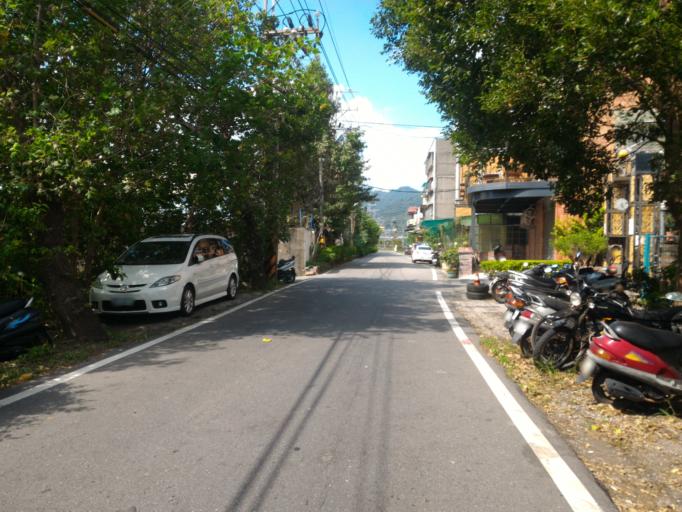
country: TW
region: Taipei
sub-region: Taipei
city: Banqiao
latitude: 24.9631
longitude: 121.4004
